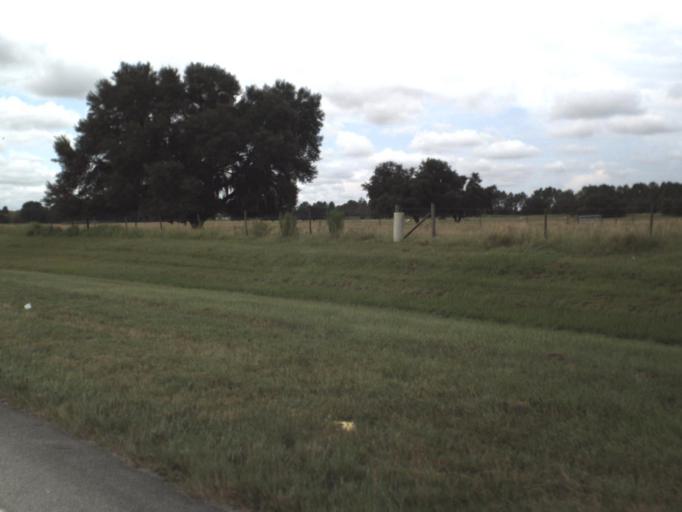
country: US
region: Florida
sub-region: Polk County
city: Fort Meade
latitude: 27.7376
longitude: -81.8016
